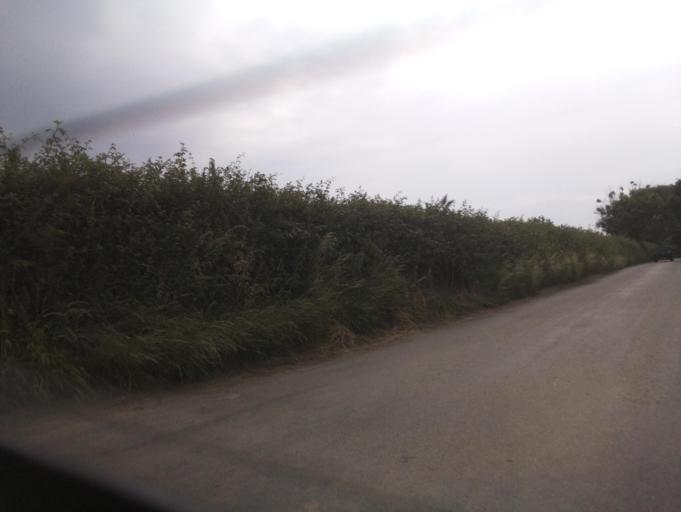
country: GB
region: England
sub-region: Devon
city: Colyton
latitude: 50.7086
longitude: -3.1133
